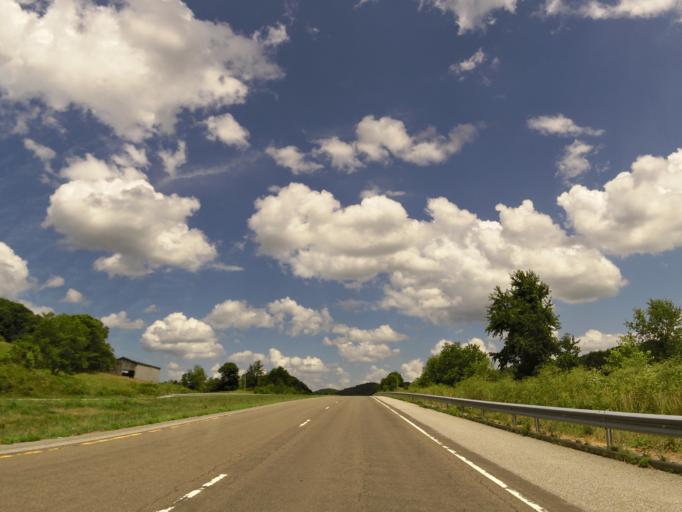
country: US
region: Kentucky
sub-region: Harlan County
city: Harlan
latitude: 36.6794
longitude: -83.3616
